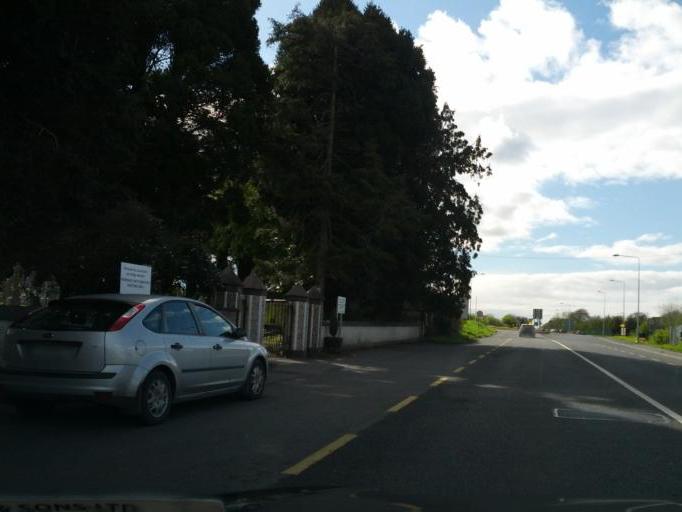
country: IE
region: Leinster
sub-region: Kildare
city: Kilcock
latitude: 53.4063
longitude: -6.6847
